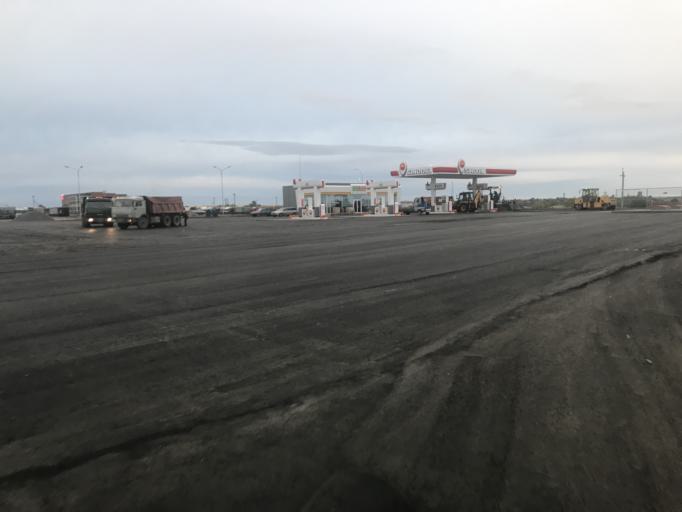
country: KZ
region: Batys Qazaqstan
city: Peremetnoe
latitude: 51.6061
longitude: 51.0754
